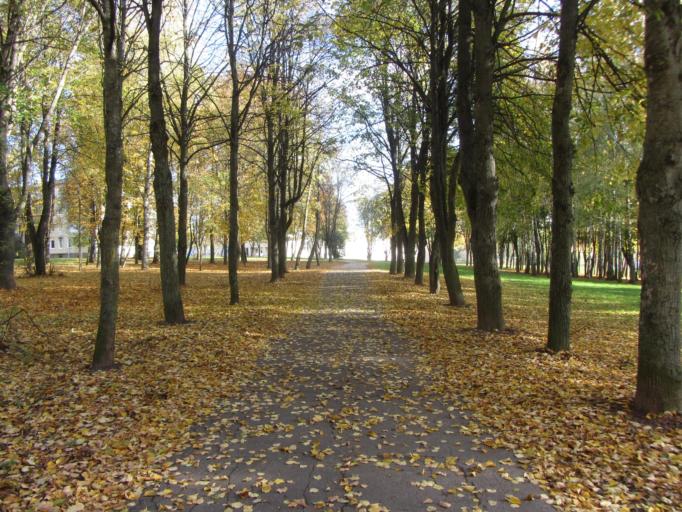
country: LT
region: Vilnius County
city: Elektrenai
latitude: 54.7827
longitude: 24.6635
